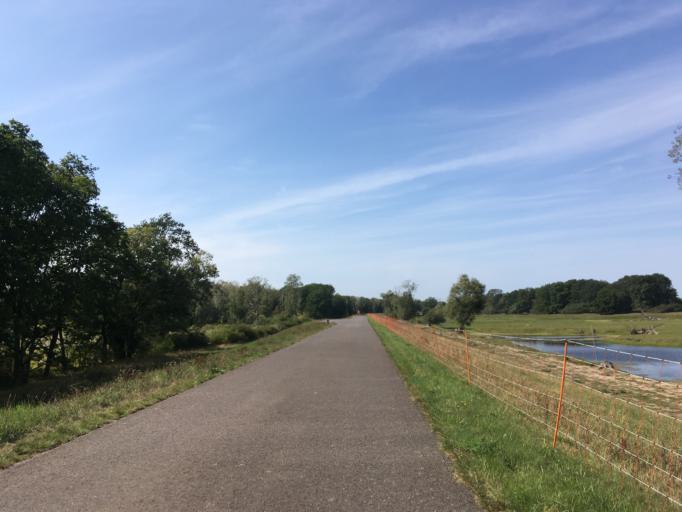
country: DE
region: Brandenburg
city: Neuzelle
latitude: 52.0922
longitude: 14.7079
